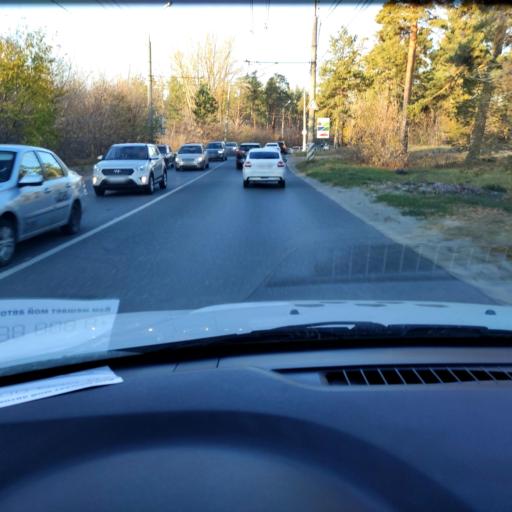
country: RU
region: Samara
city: Tol'yatti
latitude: 53.4780
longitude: 49.3631
